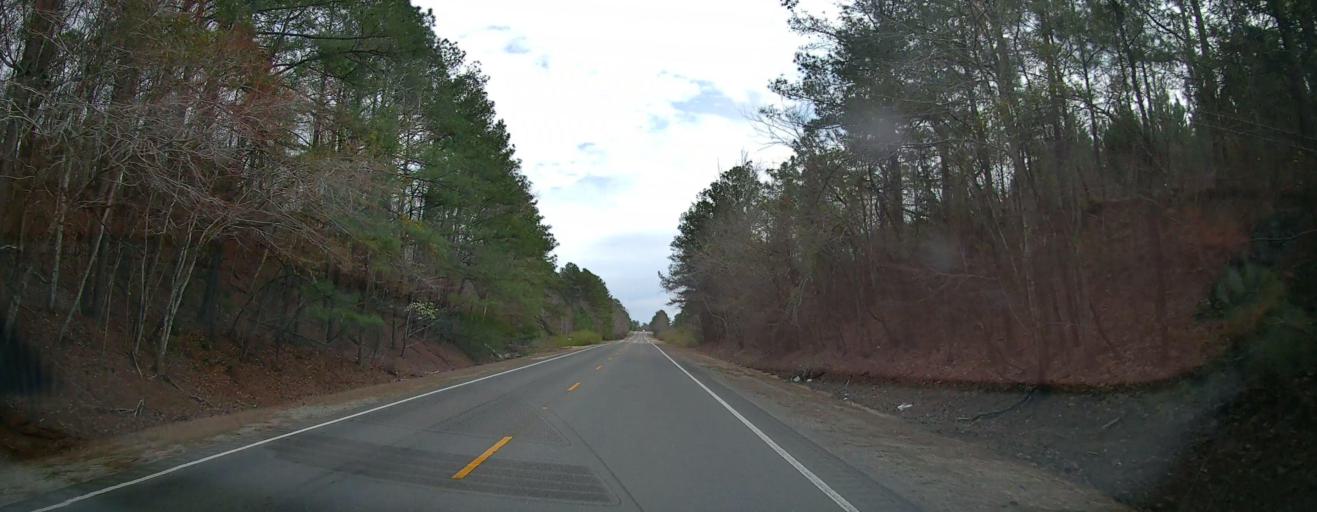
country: US
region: Alabama
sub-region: Marion County
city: Guin
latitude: 34.0441
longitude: -87.9578
